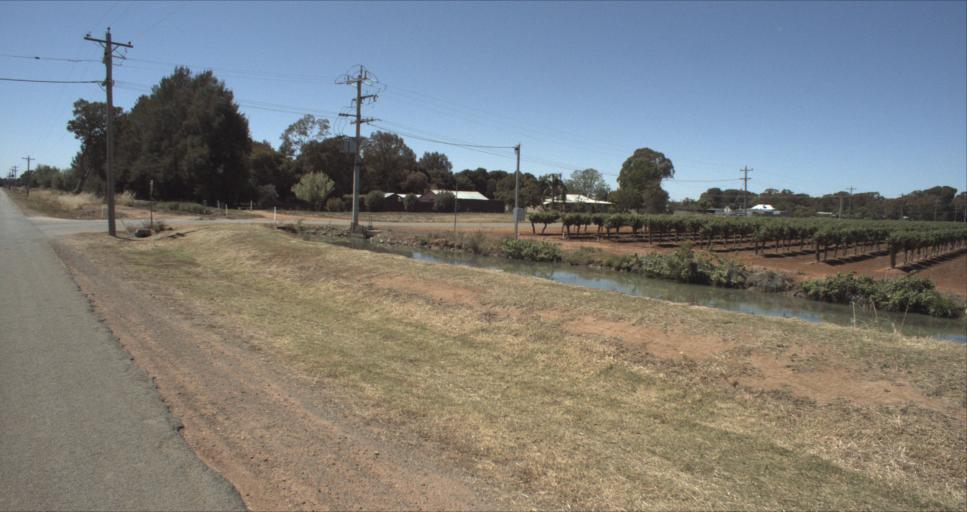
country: AU
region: New South Wales
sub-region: Leeton
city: Leeton
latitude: -34.5309
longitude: 146.3290
